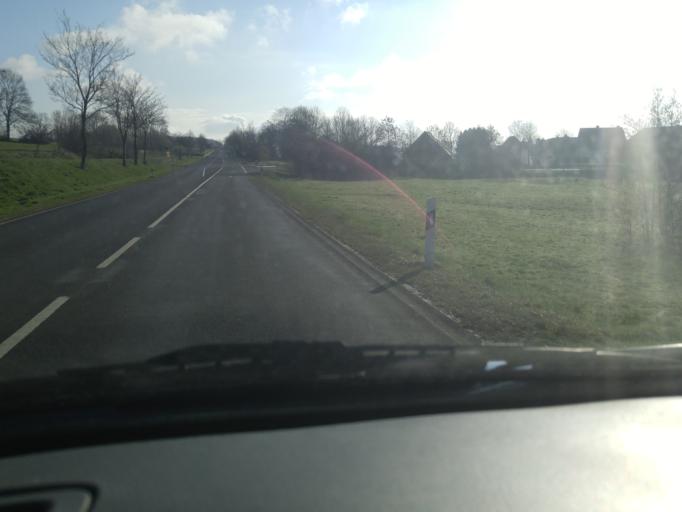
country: DE
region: Hesse
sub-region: Regierungsbezirk Giessen
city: Lautertal
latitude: 50.5878
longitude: 9.2837
